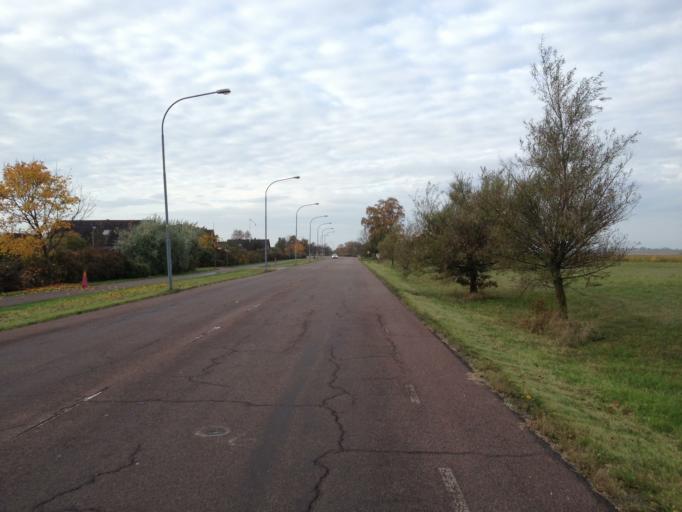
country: SE
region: Skane
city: Bjarred
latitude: 55.7308
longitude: 13.0116
